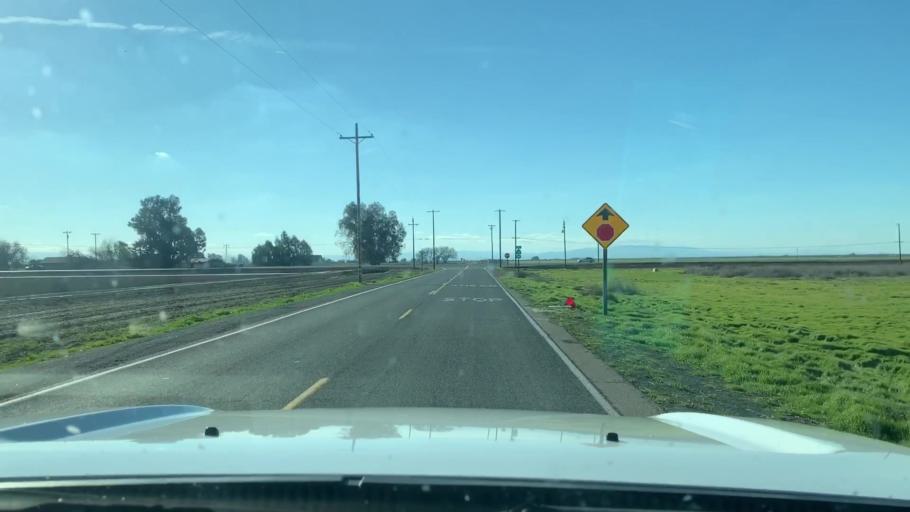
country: US
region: California
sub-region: Kings County
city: Stratford
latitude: 36.2115
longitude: -119.8140
